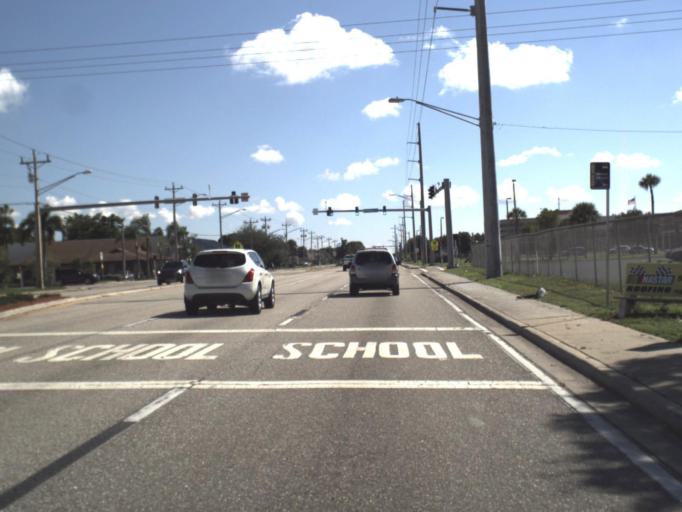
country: US
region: Florida
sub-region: Lee County
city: Lochmoor Waterway Estates
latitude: 26.6451
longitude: -81.9411
